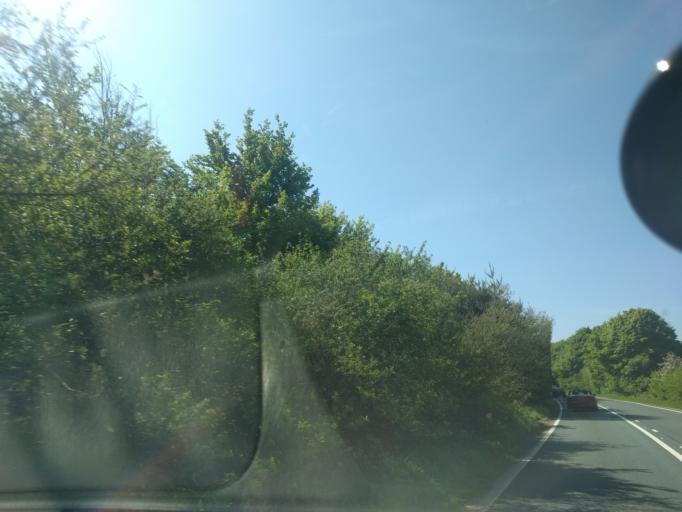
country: GB
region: England
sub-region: Somerset
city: Ilchester
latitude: 51.0302
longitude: -2.6619
